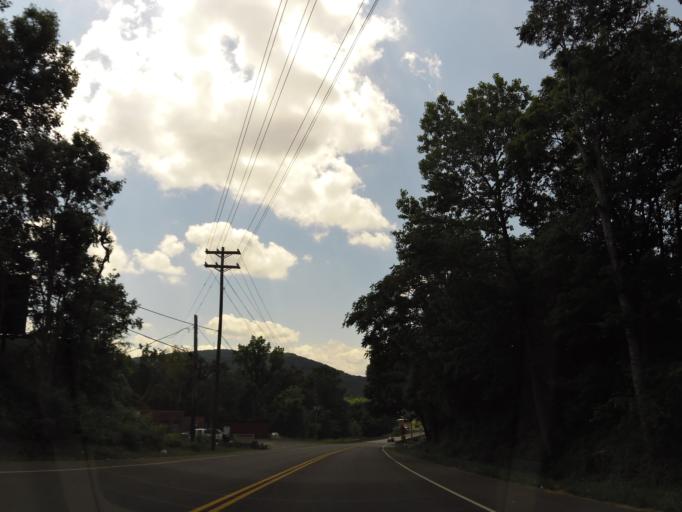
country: US
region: Tennessee
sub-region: Rhea County
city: Dayton
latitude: 35.4987
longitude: -85.0204
